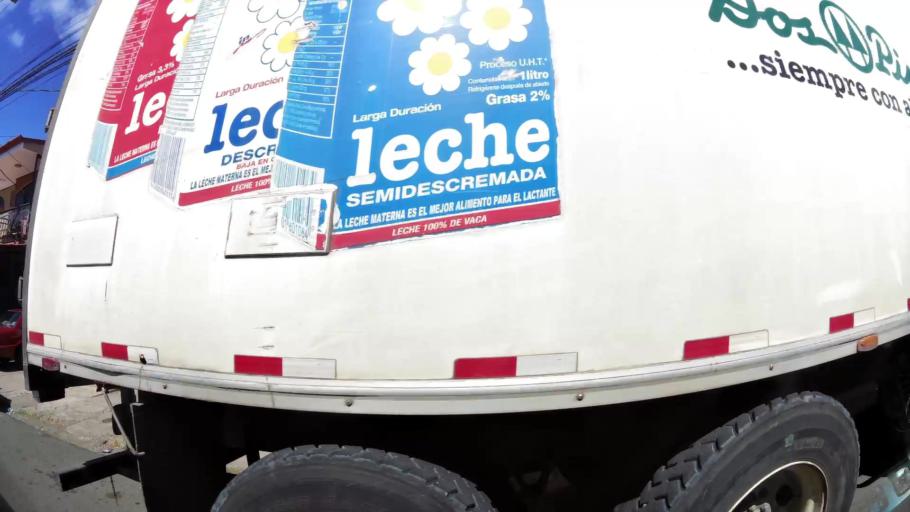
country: CR
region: Guanacaste
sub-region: Canton de Canas
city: Canas
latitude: 10.4258
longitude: -85.0922
